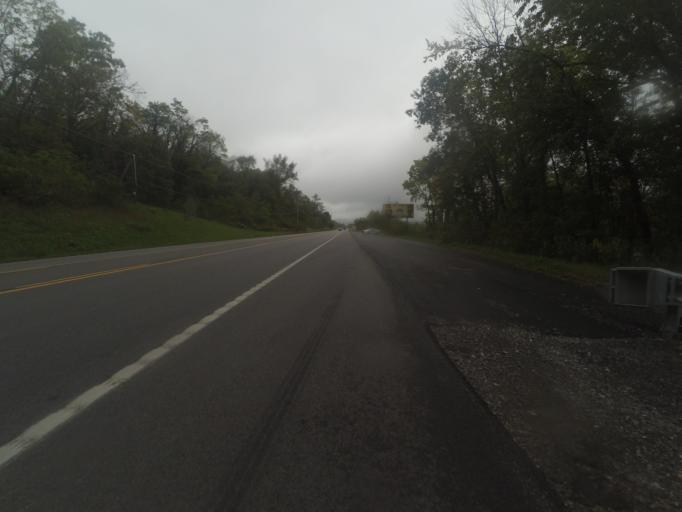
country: US
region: Pennsylvania
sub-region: Huntingdon County
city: McConnellstown
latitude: 40.5414
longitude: -78.0903
